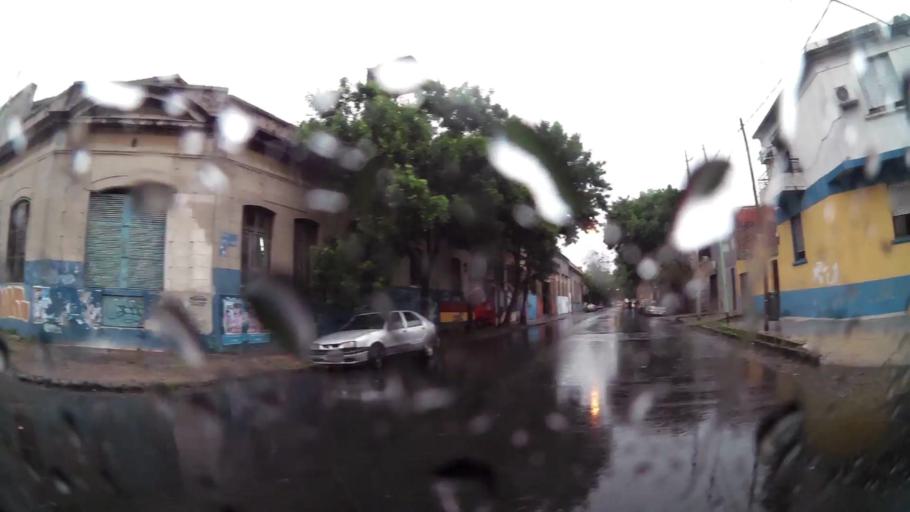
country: AR
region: Buenos Aires
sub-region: Partido de Avellaneda
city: Avellaneda
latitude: -34.6411
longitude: -58.3643
